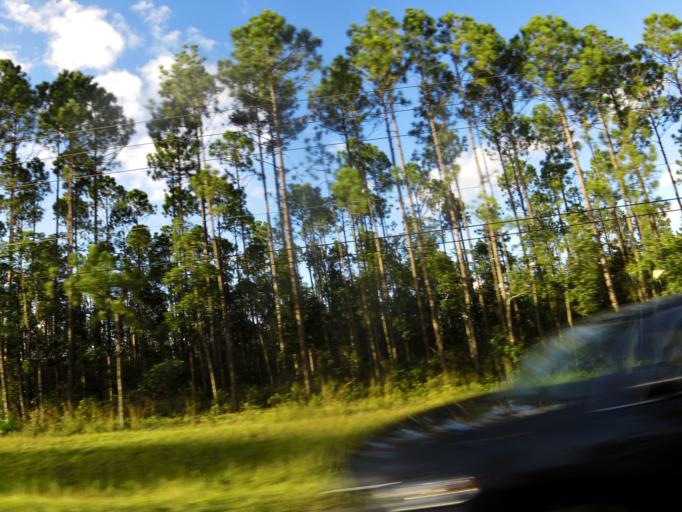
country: US
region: Florida
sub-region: Saint Johns County
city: Fruit Cove
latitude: 30.0469
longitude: -81.5642
